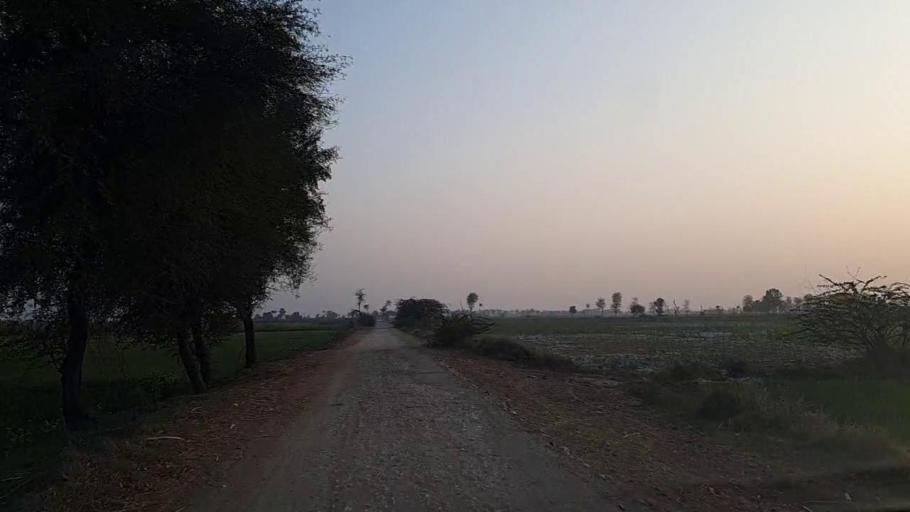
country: PK
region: Sindh
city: Daur
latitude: 26.4404
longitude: 68.3489
